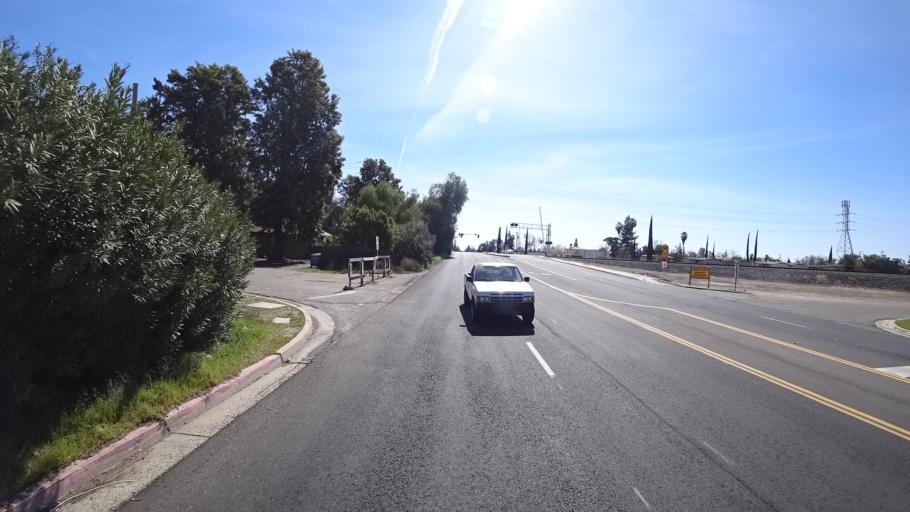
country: US
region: California
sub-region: Fresno County
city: Fresno
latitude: 36.7877
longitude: -119.8086
